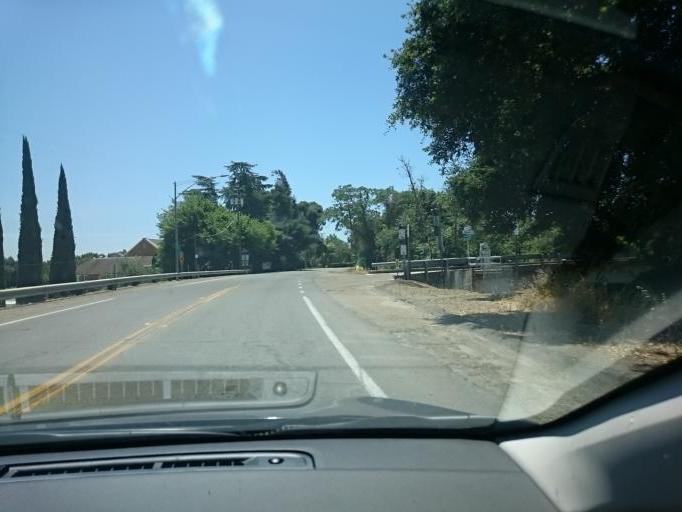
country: US
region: California
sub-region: Sacramento County
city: Walnut Grove
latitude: 38.2378
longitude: -121.5169
